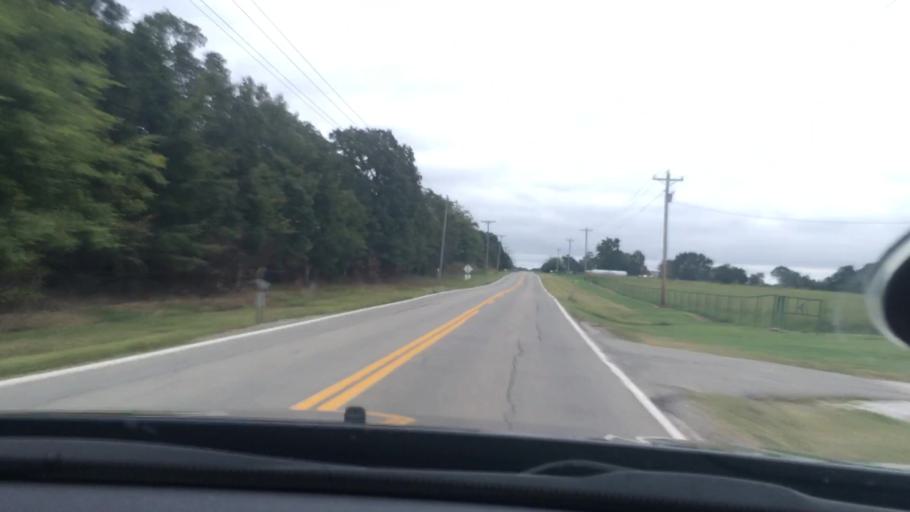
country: US
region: Oklahoma
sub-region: Sequoyah County
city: Vian
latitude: 35.6097
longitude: -94.9964
